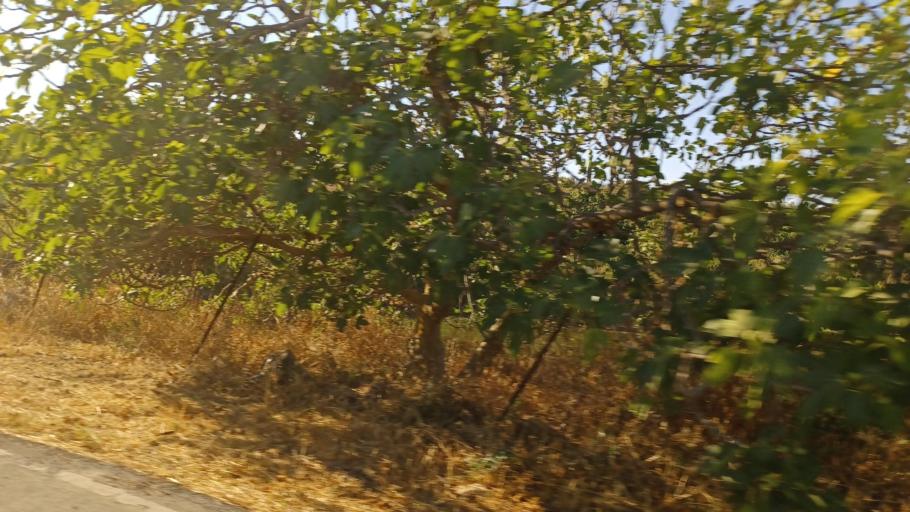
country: CY
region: Pafos
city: Tala
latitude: 34.9276
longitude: 32.5386
